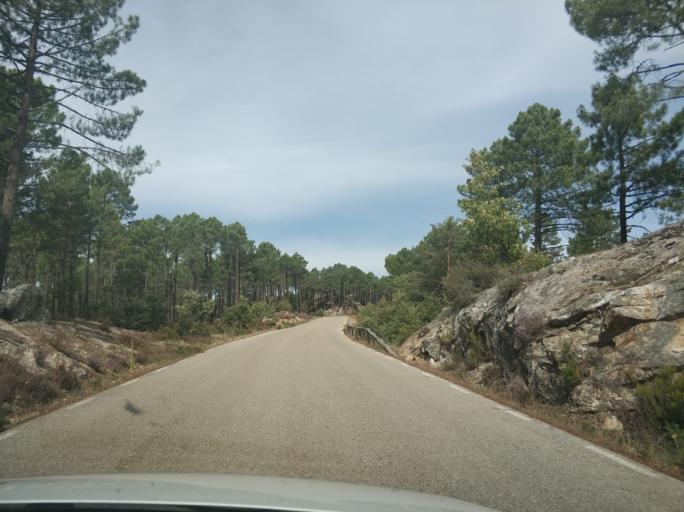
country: ES
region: Castille and Leon
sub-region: Provincia de Soria
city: Duruelo de la Sierra
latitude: 41.8866
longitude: -2.9383
